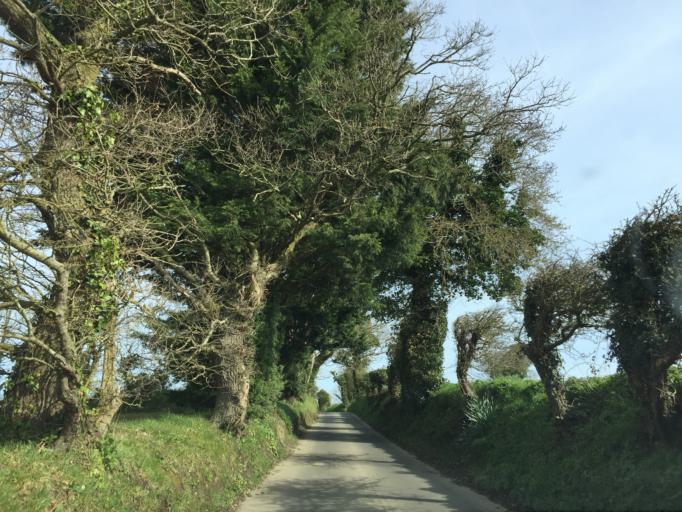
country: JE
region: St Helier
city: Saint Helier
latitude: 49.2205
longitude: -2.1396
